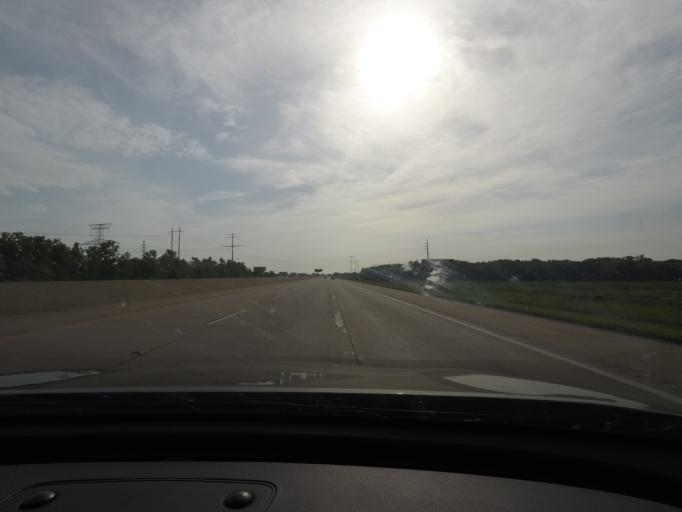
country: US
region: Missouri
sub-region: Saint Charles County
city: Saint Charles
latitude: 38.8215
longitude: -90.5440
